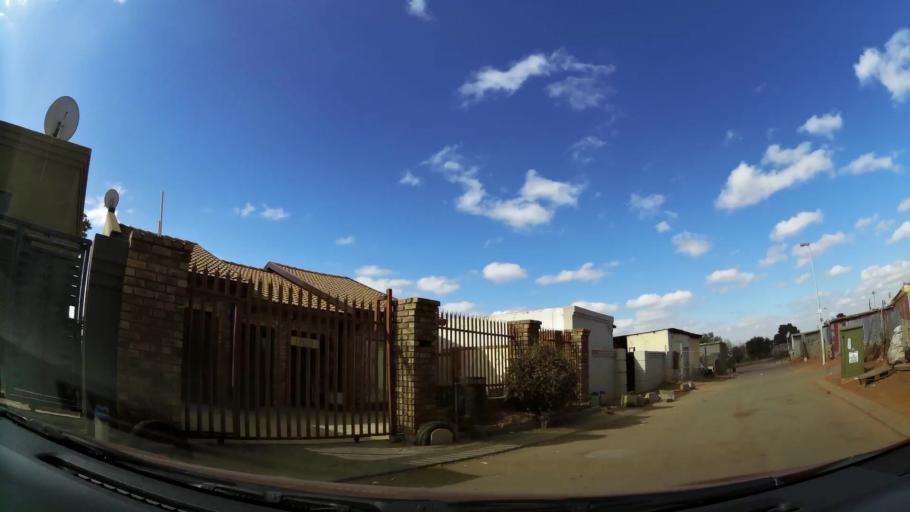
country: ZA
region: Gauteng
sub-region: City of Johannesburg Metropolitan Municipality
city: Modderfontein
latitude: -26.0361
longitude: 28.1769
